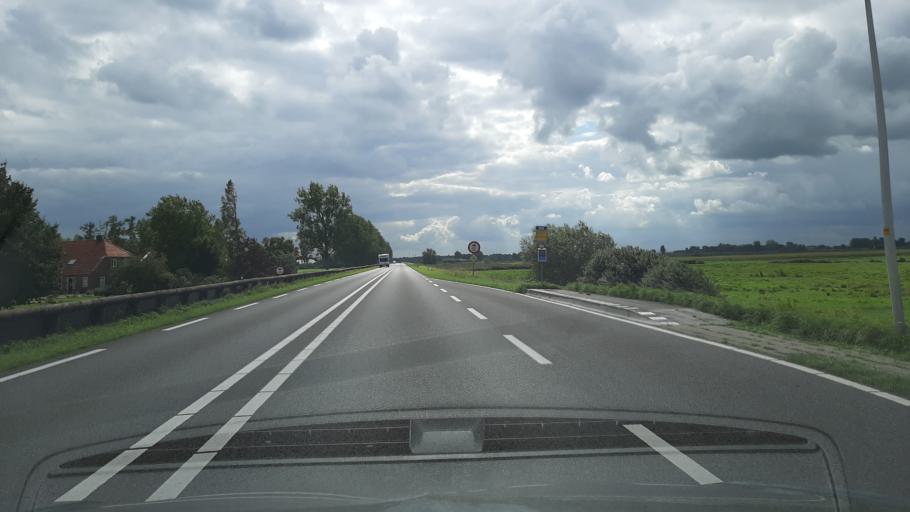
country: NL
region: Overijssel
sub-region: Gemeente Zwartewaterland
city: Hasselt
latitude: 52.6223
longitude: 6.0885
